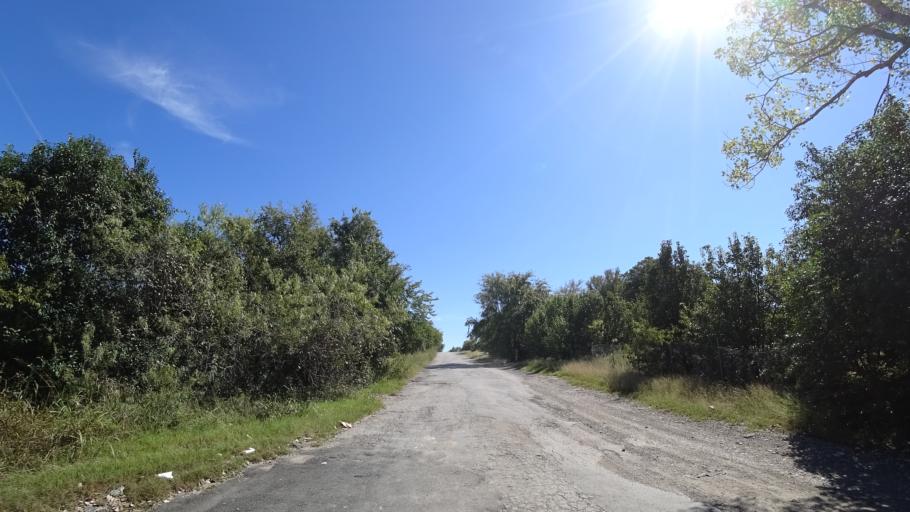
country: US
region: Texas
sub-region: Travis County
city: Austin
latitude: 30.2130
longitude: -97.6891
